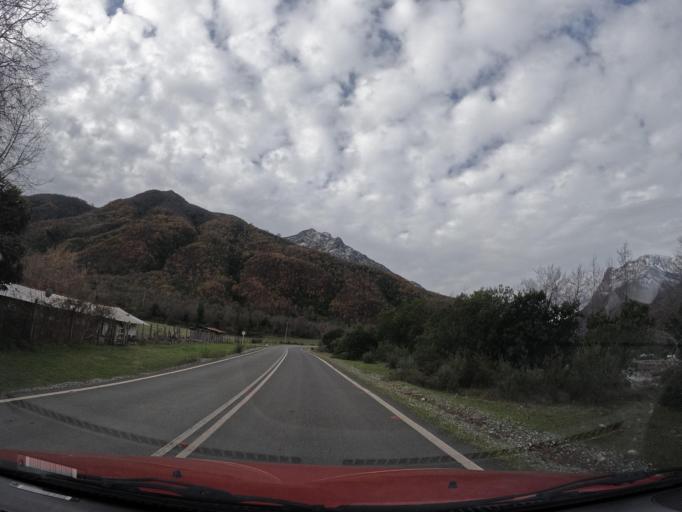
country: CL
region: Maule
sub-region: Provincia de Linares
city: Colbun
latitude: -35.8590
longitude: -71.2477
